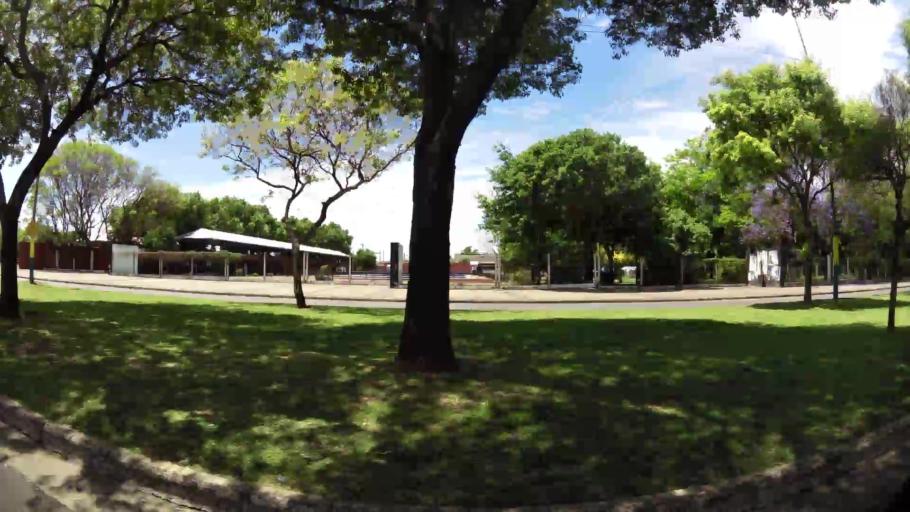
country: AR
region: Santa Fe
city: Gobernador Galvez
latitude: -32.9948
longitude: -60.6252
